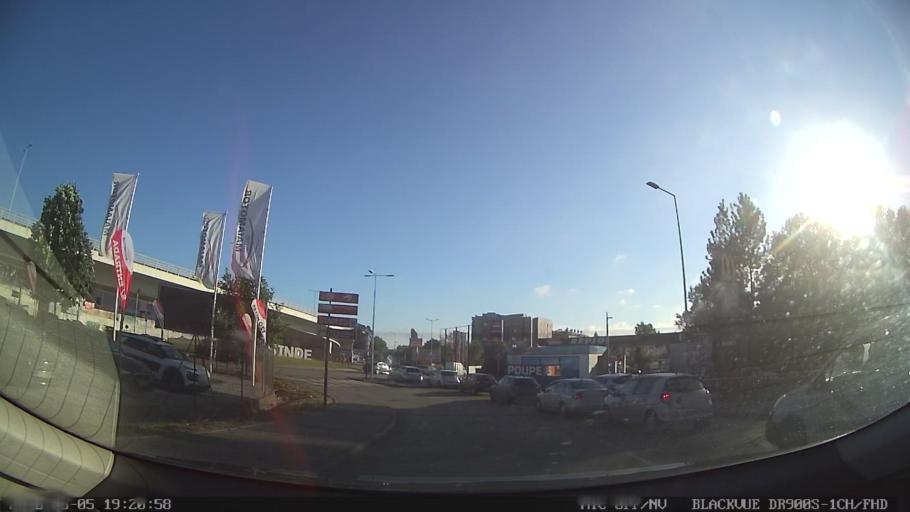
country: PT
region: Porto
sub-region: Gondomar
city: Baguim do Monte
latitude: 41.2055
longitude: -8.5478
